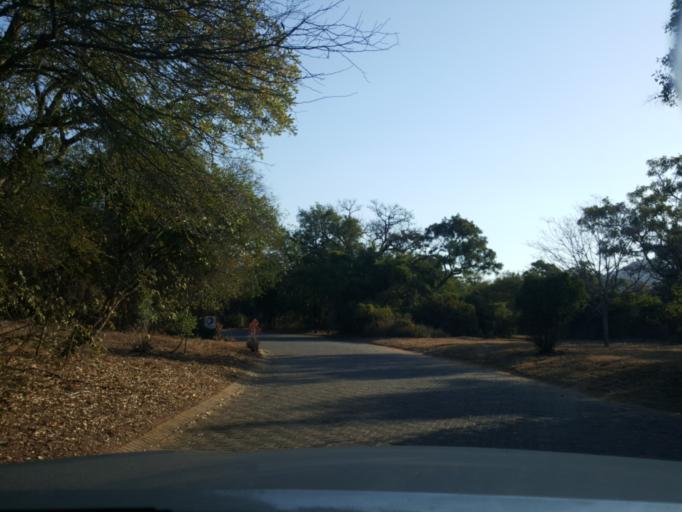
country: SZ
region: Hhohho
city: Ntfonjeni
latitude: -25.4265
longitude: 31.4478
